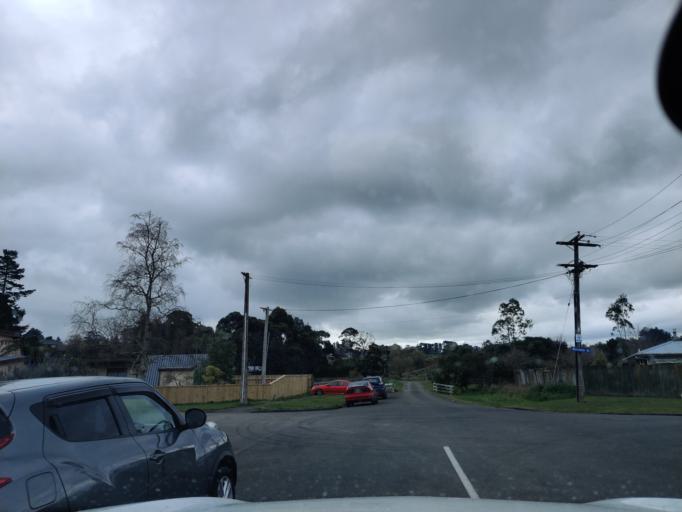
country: NZ
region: Manawatu-Wanganui
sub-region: Palmerston North City
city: Palmerston North
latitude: -40.2873
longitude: 175.7500
